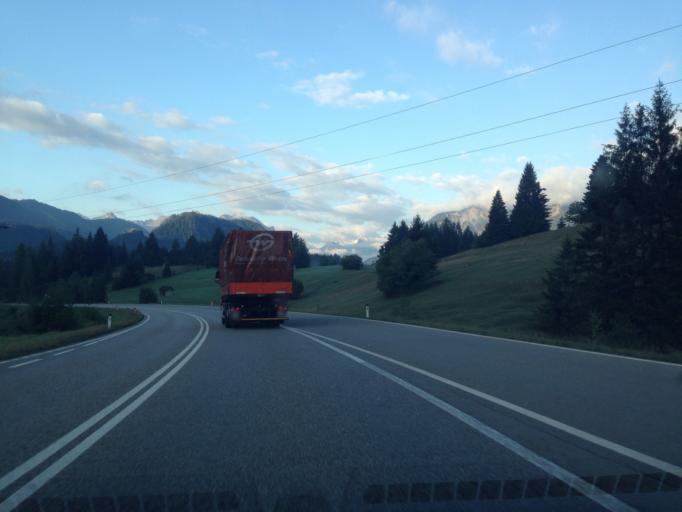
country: AT
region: Tyrol
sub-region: Politischer Bezirk Reutte
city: Breitenwang
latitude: 47.4892
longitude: 10.7447
